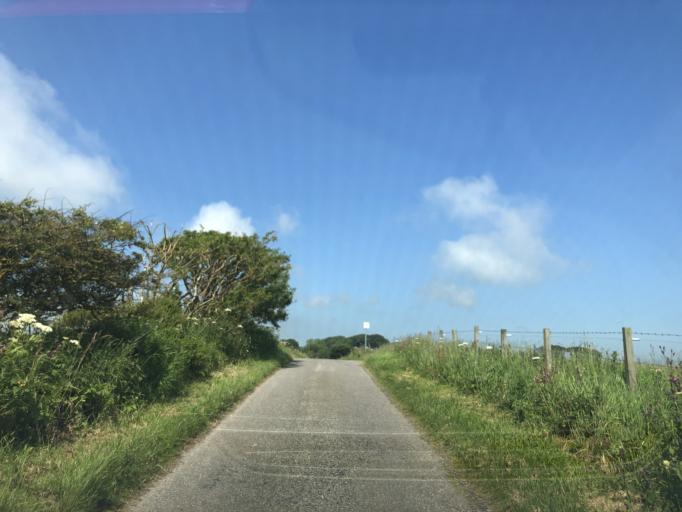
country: GB
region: Scotland
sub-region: Aberdeenshire
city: Stonehaven
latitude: 56.9141
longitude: -2.2028
